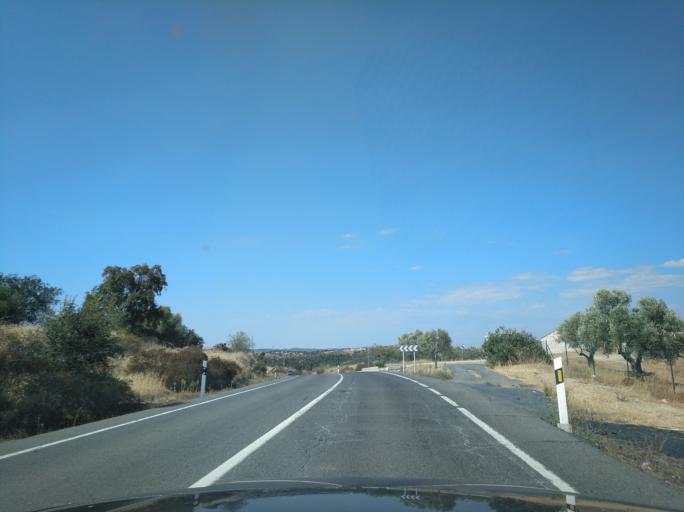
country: ES
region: Andalusia
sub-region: Provincia de Huelva
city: Alosno
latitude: 37.4975
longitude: -7.1318
